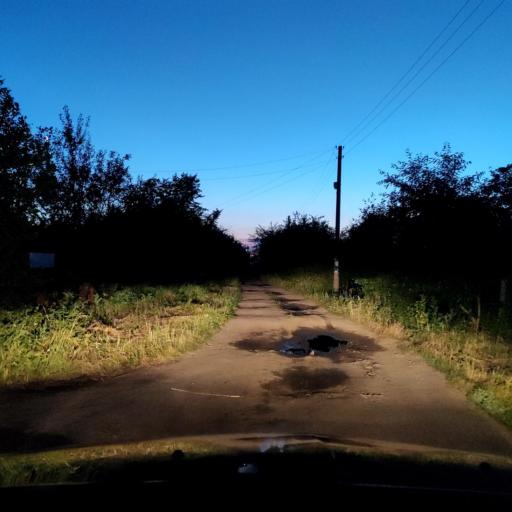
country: RU
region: Voronezj
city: Podgornoye
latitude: 51.8033
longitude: 39.2228
